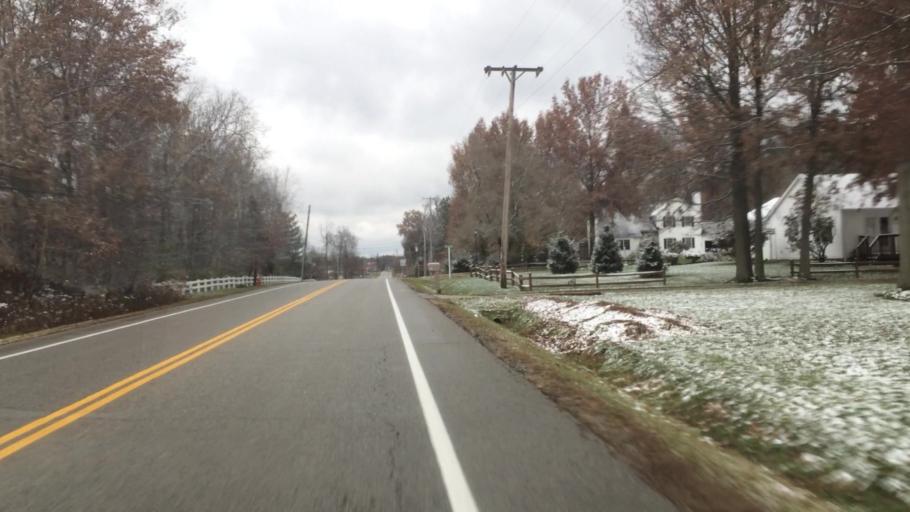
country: US
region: Ohio
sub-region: Summit County
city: Macedonia
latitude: 41.3066
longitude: -81.5328
